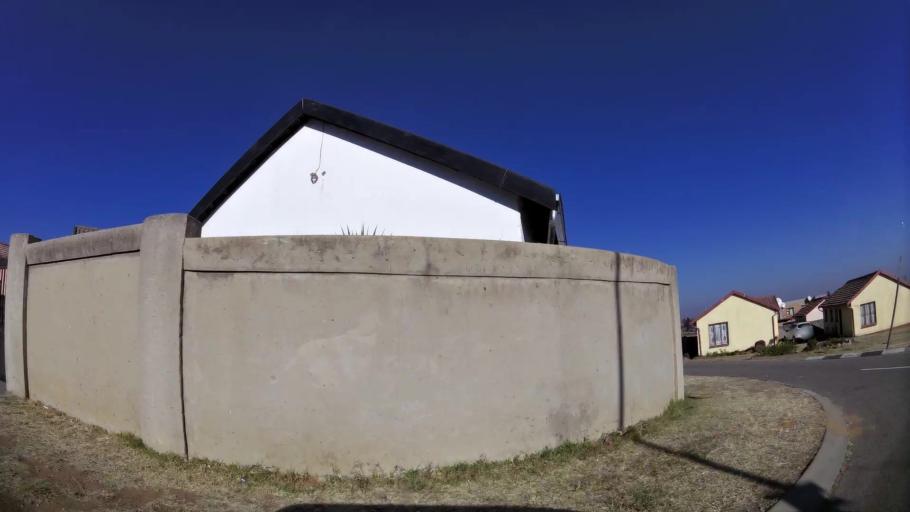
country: ZA
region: Gauteng
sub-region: City of Johannesburg Metropolitan Municipality
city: Modderfontein
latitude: -26.0408
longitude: 28.1592
